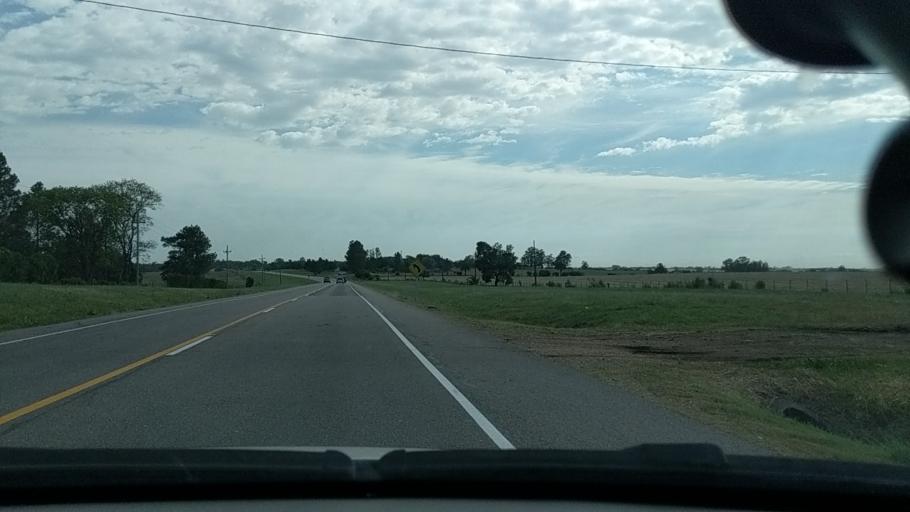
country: UY
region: Florida
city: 25 de Mayo
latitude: -34.2943
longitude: -56.2241
